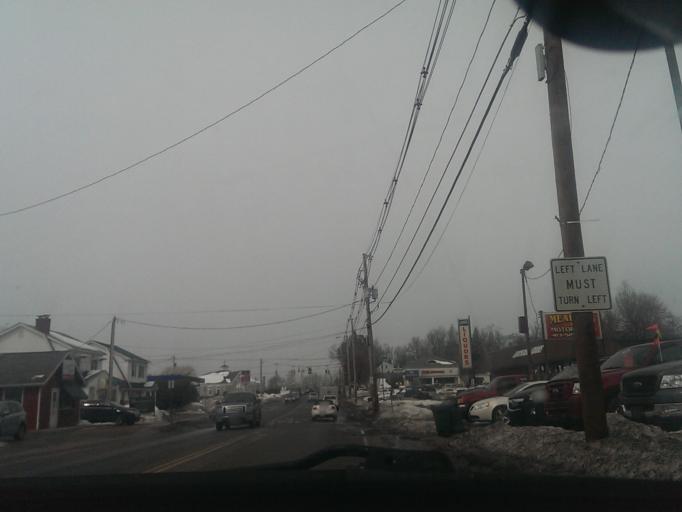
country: US
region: Massachusetts
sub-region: Hampden County
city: East Longmeadow
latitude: 42.0714
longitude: -72.5175
